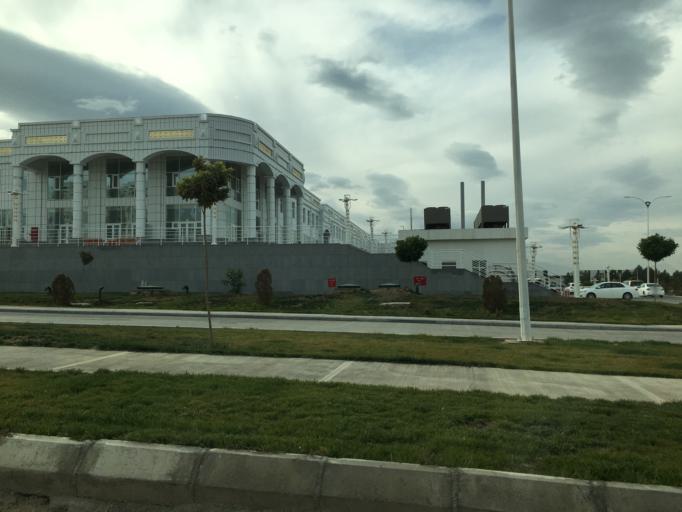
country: TM
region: Ahal
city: Ashgabat
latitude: 37.9020
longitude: 58.4151
